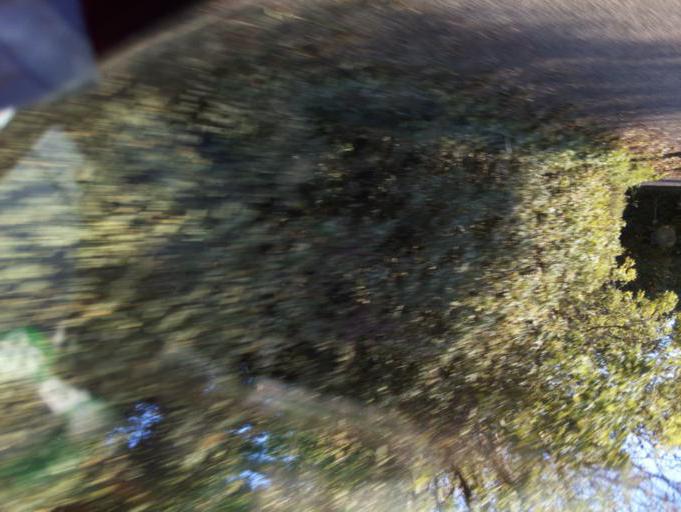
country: GB
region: England
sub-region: Worcestershire
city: Upton upon Severn
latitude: 52.0038
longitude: -2.2394
